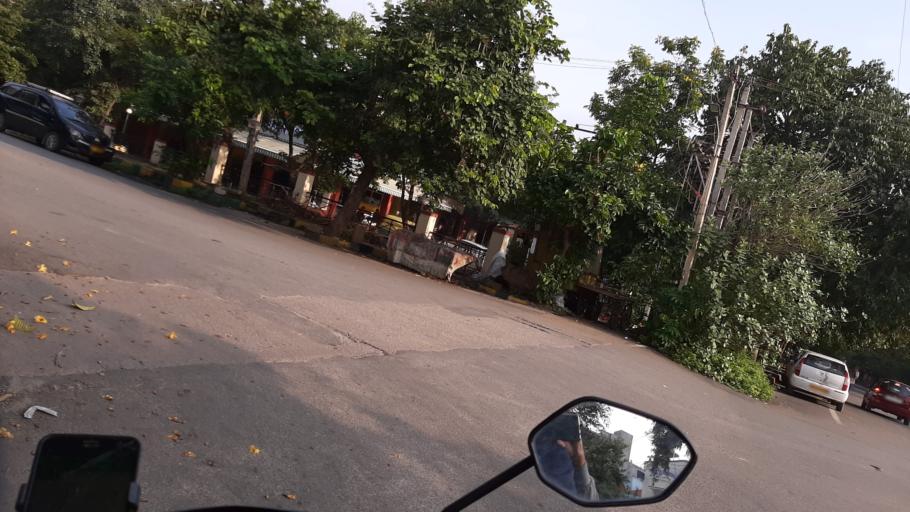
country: IN
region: Karnataka
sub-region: Bangalore Urban
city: Bangalore
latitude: 12.9793
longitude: 77.5118
